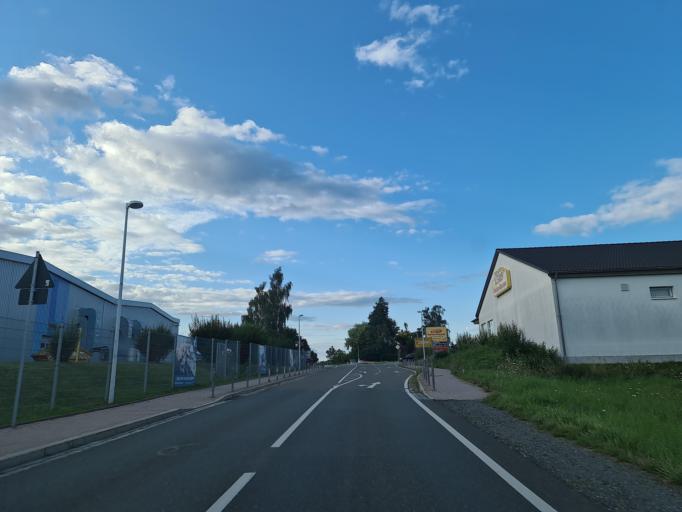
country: DE
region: Saxony
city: Pausa
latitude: 50.5868
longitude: 11.9987
